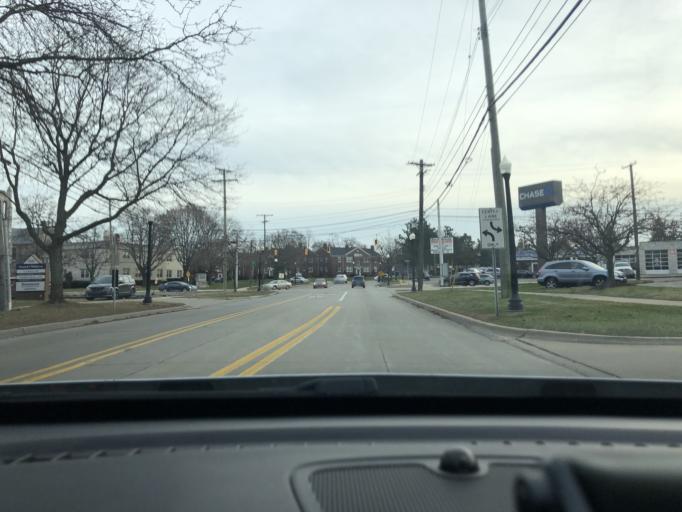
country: US
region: Michigan
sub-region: Wayne County
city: Dearborn Heights
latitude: 42.3030
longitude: -83.2427
